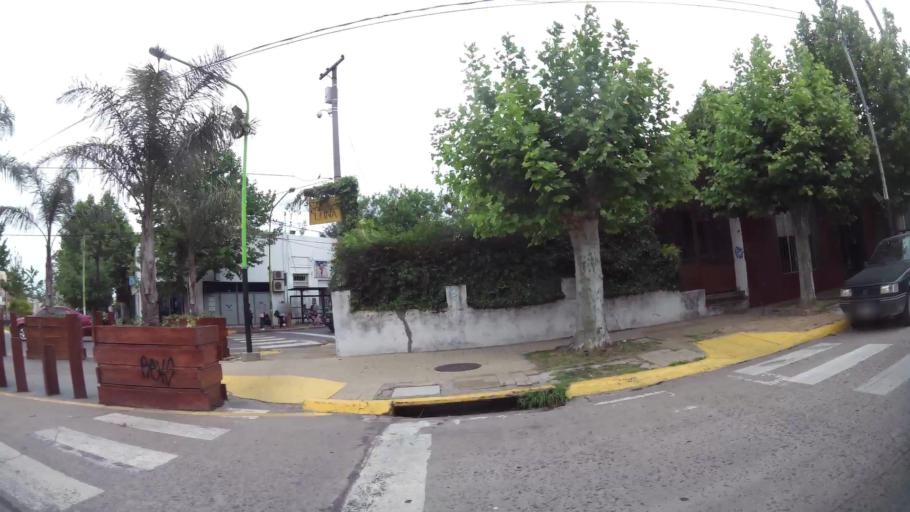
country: AR
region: Buenos Aires
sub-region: Partido de Campana
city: Campana
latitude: -34.1634
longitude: -58.9582
